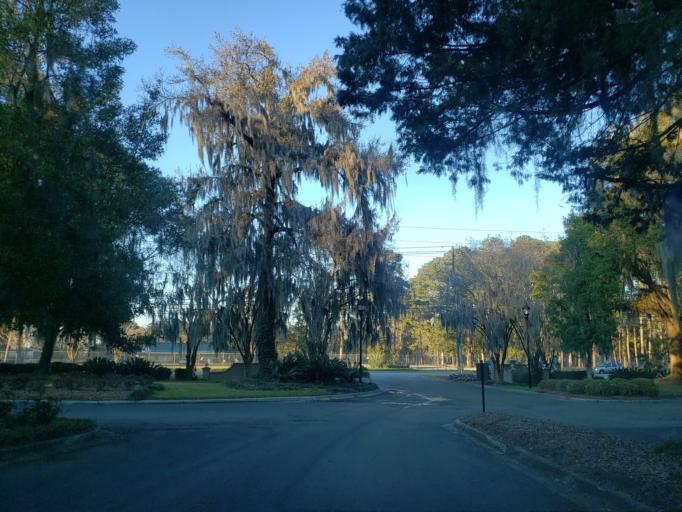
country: US
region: Georgia
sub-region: Chatham County
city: Montgomery
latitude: 32.0004
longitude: -81.1336
